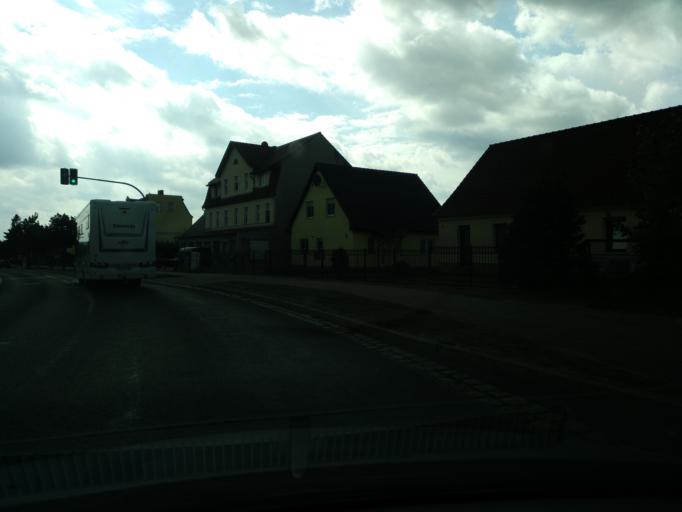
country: DE
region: Brandenburg
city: Woltersdorf
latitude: 52.4798
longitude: 13.7734
